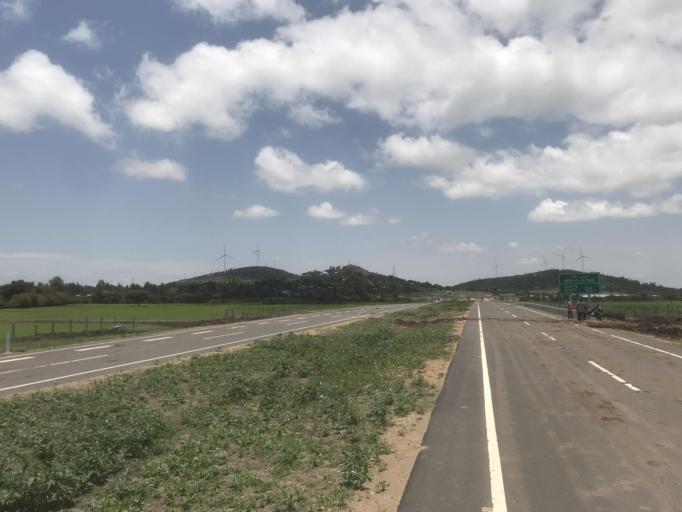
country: ET
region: Oromiya
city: Mojo
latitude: 8.5745
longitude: 39.1696
